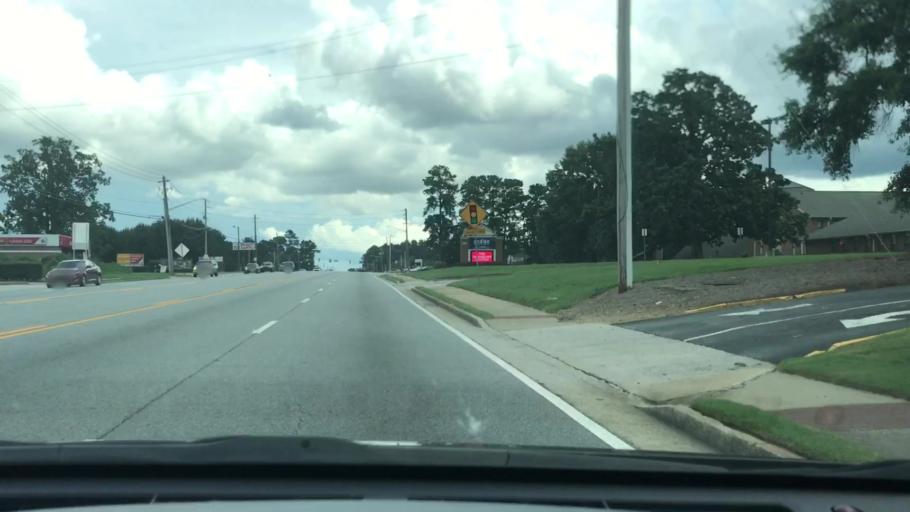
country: US
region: Georgia
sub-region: Gwinnett County
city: Lawrenceville
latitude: 33.9436
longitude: -83.9841
